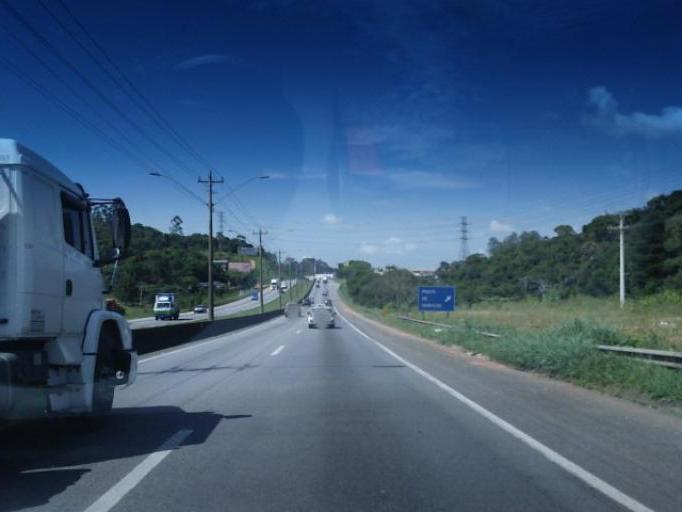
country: BR
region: Sao Paulo
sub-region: Itapecerica Da Serra
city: Itapecerica da Serra
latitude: -23.7122
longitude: -46.8781
